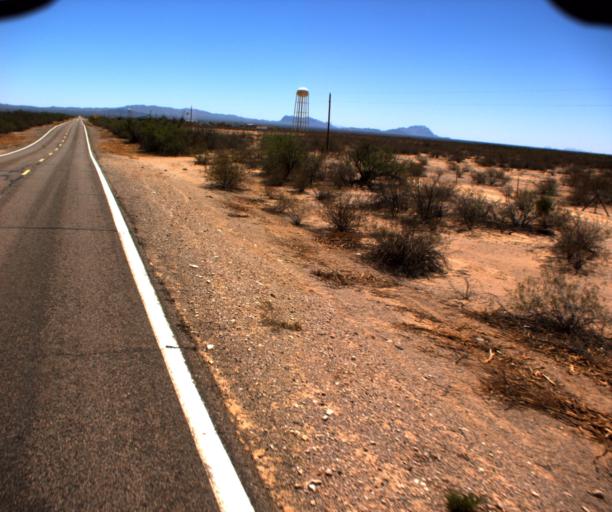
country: US
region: Arizona
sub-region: Pima County
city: Ajo
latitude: 32.1919
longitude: -112.4261
